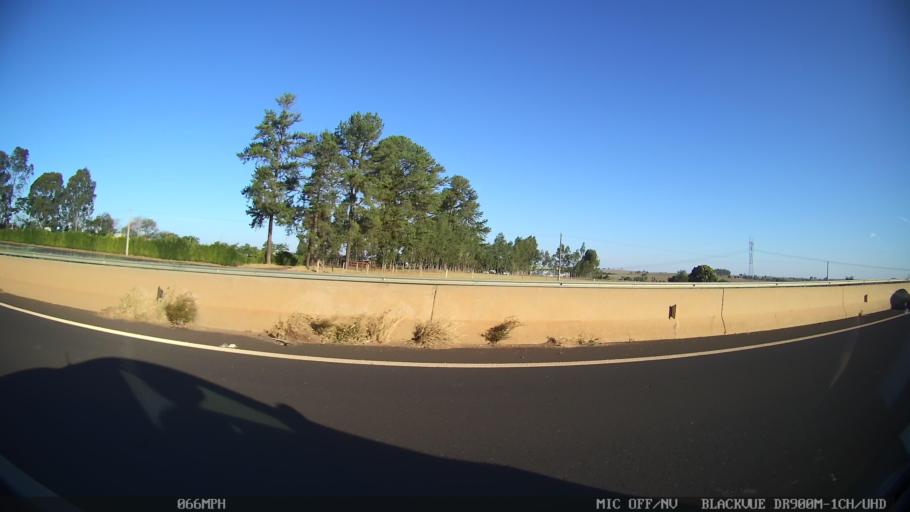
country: BR
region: Sao Paulo
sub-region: Guapiacu
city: Guapiacu
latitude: -20.7910
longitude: -49.2981
